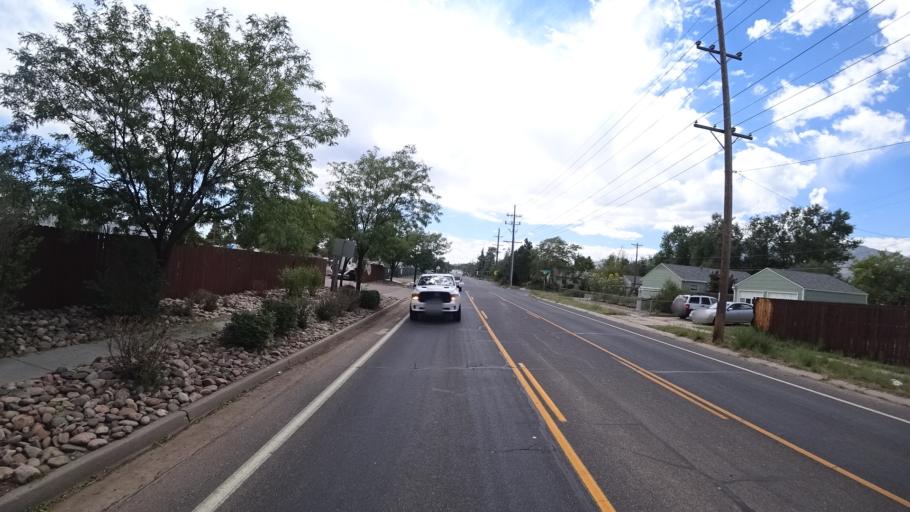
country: US
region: Colorado
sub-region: El Paso County
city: Stratmoor
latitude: 38.8008
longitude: -104.8035
